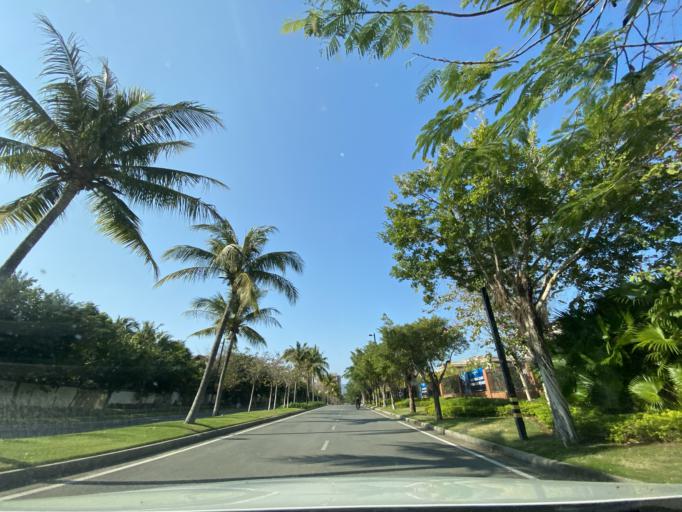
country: CN
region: Hainan
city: Yingzhou
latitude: 18.4148
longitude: 109.8894
